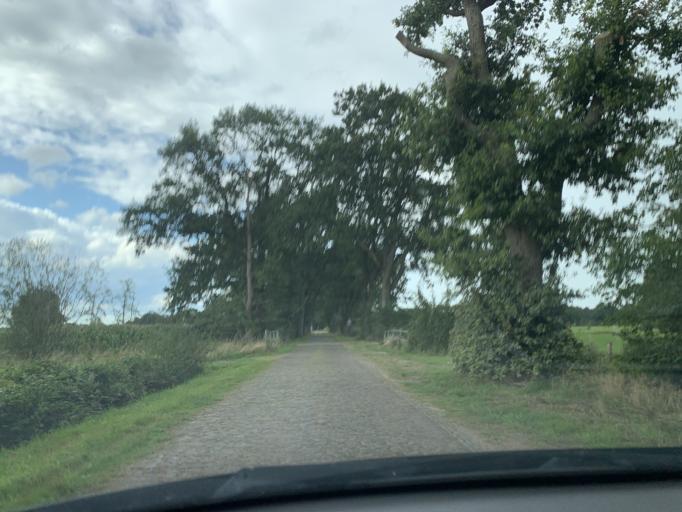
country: DE
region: Lower Saxony
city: Westerstede
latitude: 53.2741
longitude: 7.9800
